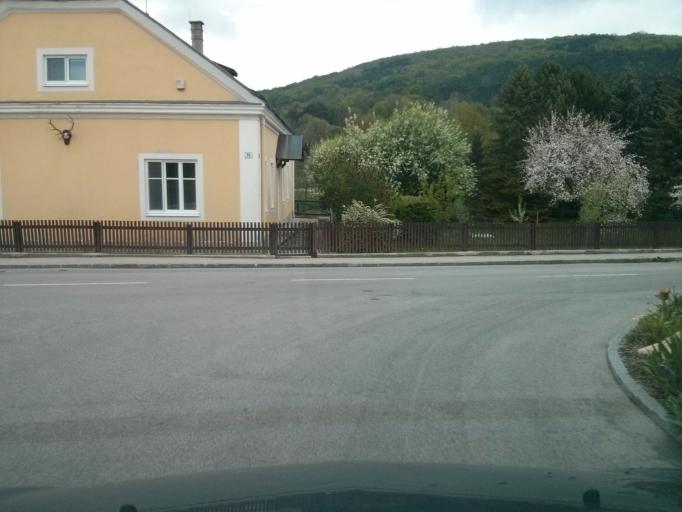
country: AT
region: Lower Austria
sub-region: Politischer Bezirk Baden
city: Hernstein
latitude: 47.8943
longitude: 16.1039
